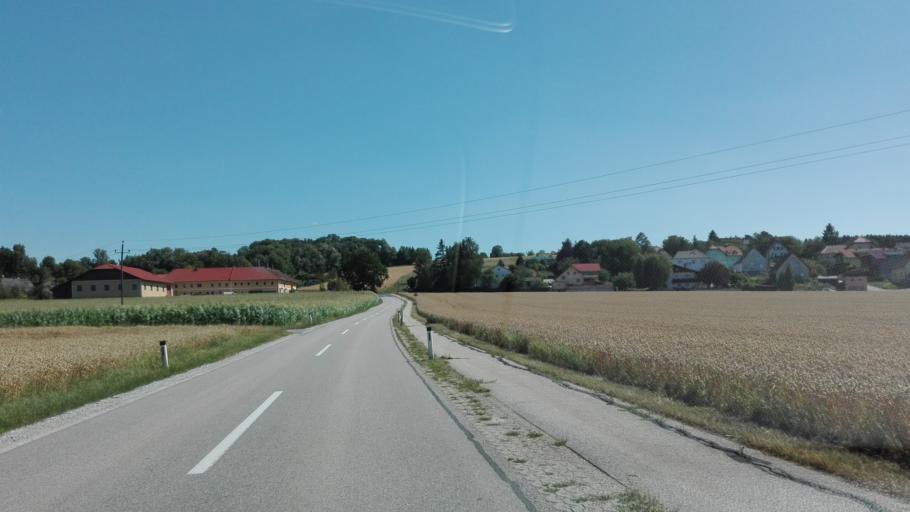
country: AT
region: Upper Austria
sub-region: Politischer Bezirk Urfahr-Umgebung
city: Goldworth
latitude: 48.2762
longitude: 14.1137
